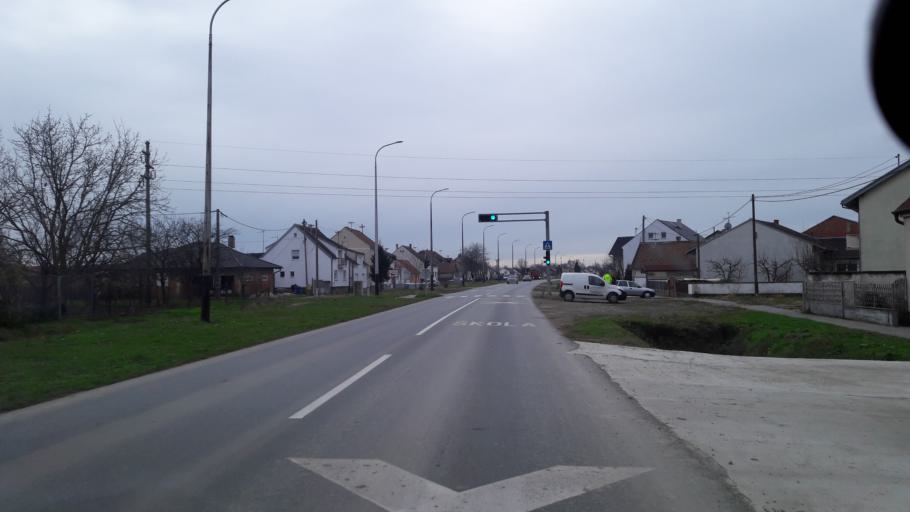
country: HR
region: Osjecko-Baranjska
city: Ovcara
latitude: 45.5123
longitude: 18.5686
